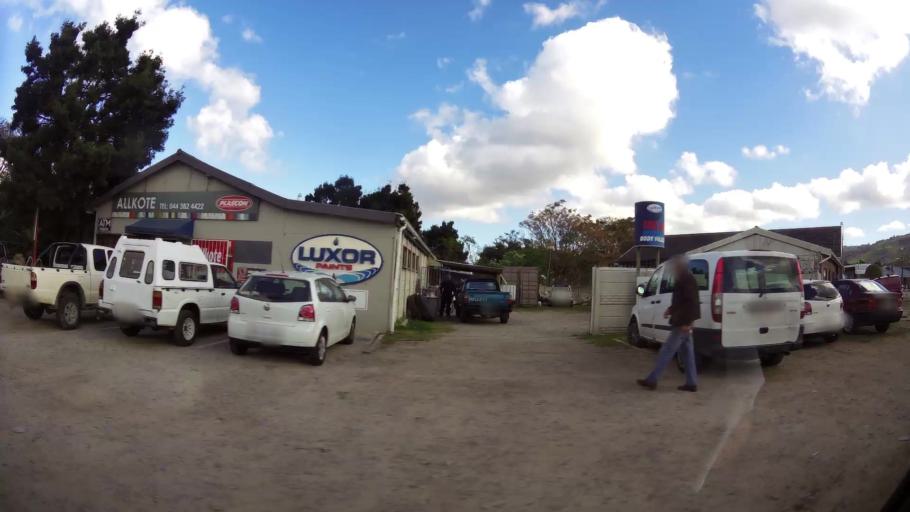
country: ZA
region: Western Cape
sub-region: Eden District Municipality
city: Knysna
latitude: -34.0468
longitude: 23.0730
